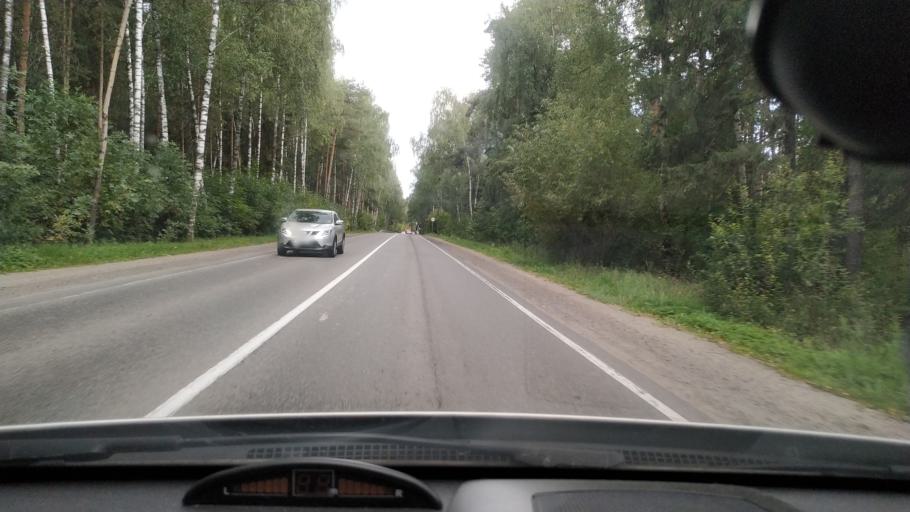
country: RU
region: Moskovskaya
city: Chornaya
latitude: 55.7803
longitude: 38.0420
